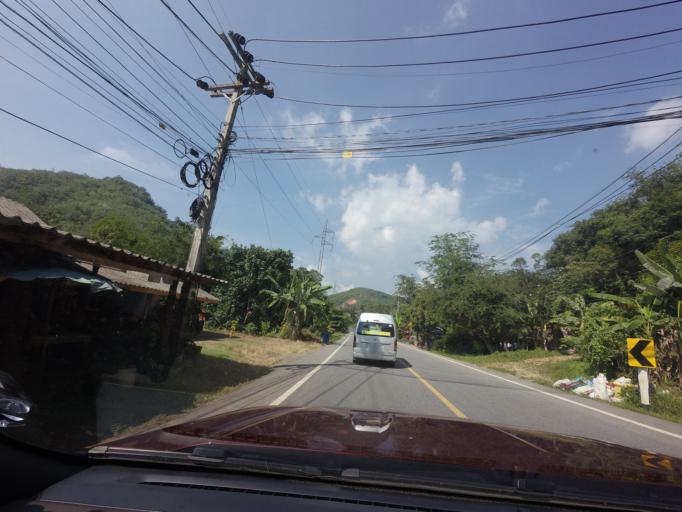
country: TH
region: Yala
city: Betong
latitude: 5.9399
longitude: 101.1874
